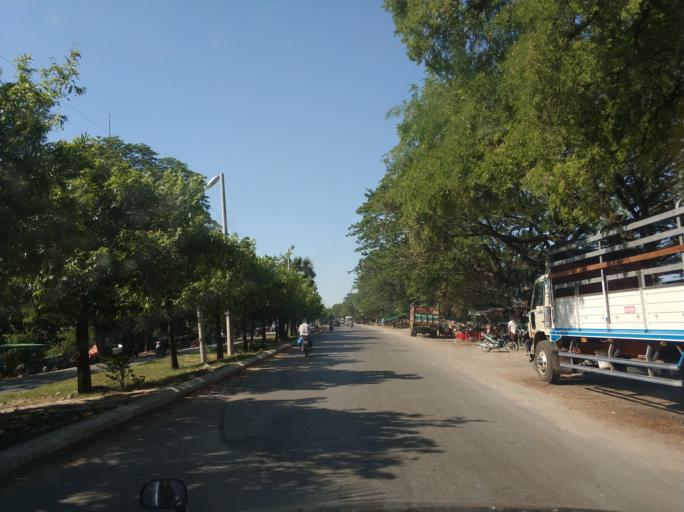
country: MM
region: Mandalay
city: Mandalay
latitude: 21.9679
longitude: 96.0563
